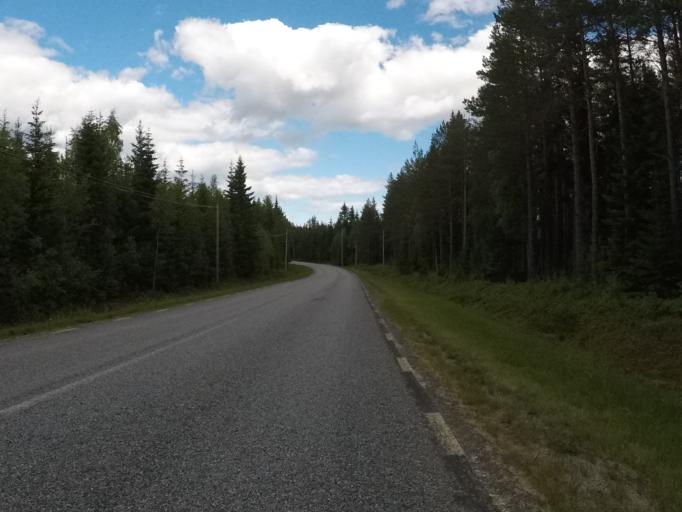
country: SE
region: Vaesterbotten
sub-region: Umea Kommun
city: Saevar
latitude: 63.9285
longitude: 20.7776
